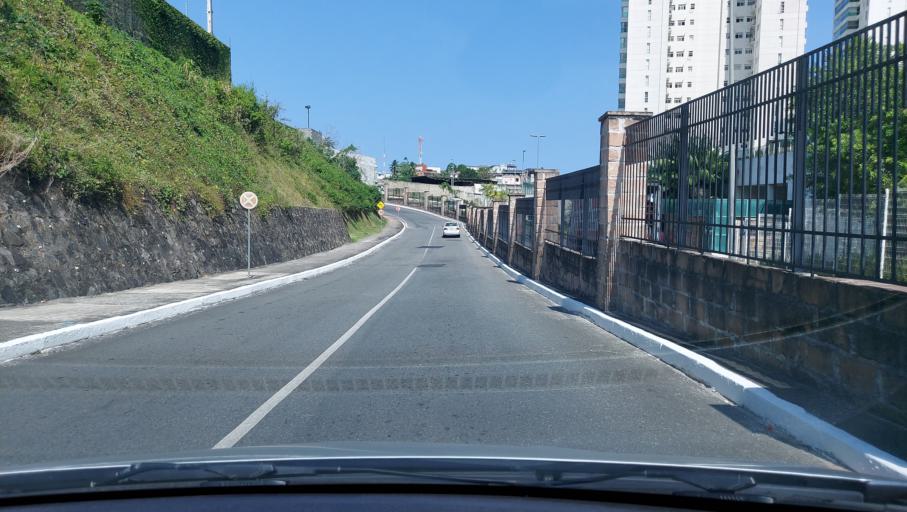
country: BR
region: Bahia
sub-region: Salvador
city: Salvador
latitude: -12.9664
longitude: -38.4728
